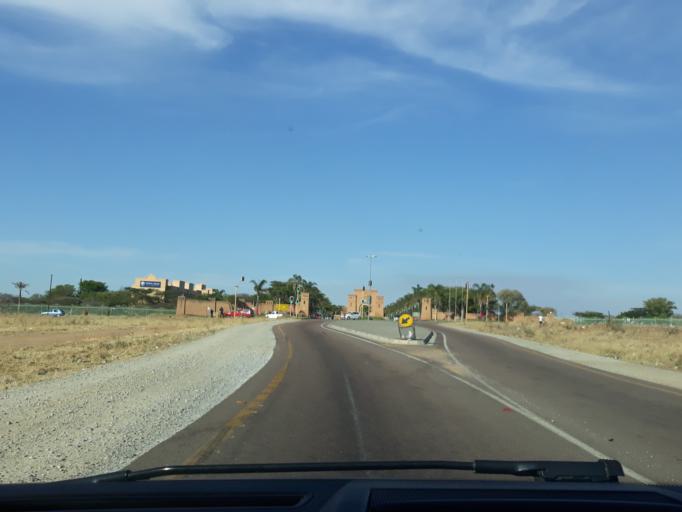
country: ZA
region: Limpopo
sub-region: Capricorn District Municipality
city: Polokwane
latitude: -23.9438
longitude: 29.4204
